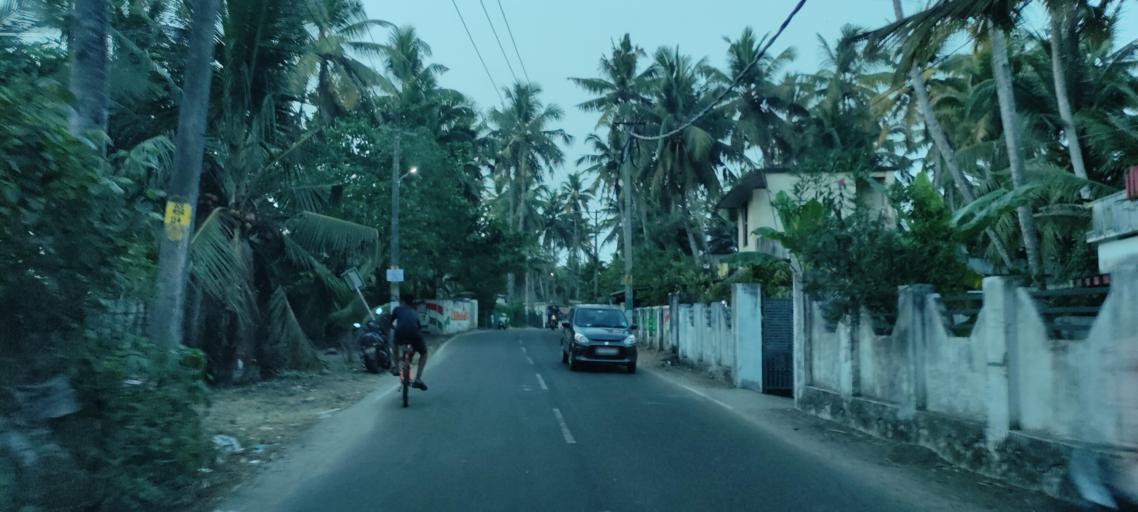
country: IN
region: Kerala
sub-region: Alappuzha
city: Kayankulam
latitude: 9.1154
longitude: 76.4729
